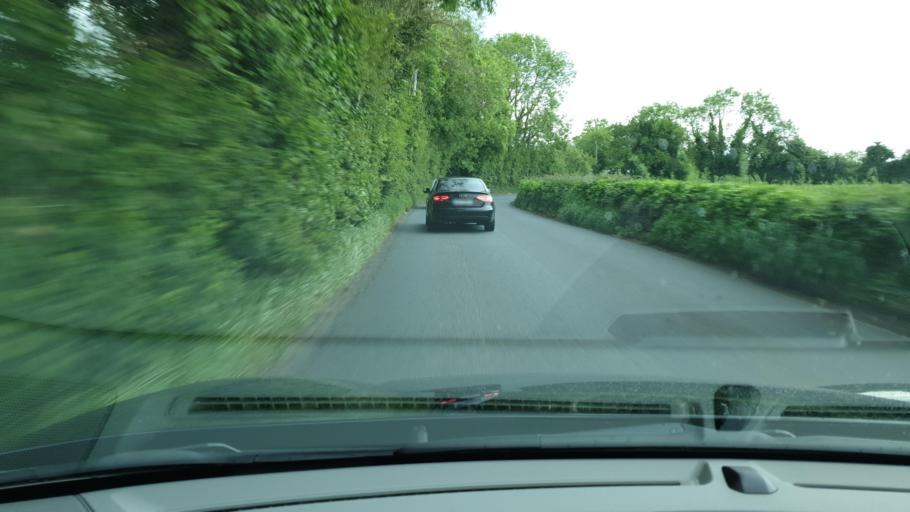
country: IE
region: Leinster
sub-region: An Mhi
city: Ashbourne
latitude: 53.5327
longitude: -6.4067
